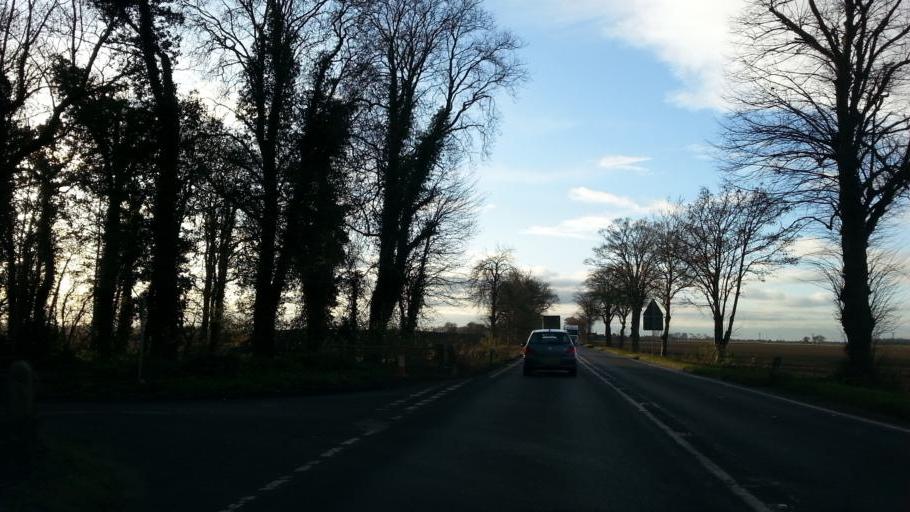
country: GB
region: England
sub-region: Peterborough
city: Thorney
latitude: 52.6169
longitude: -0.1446
